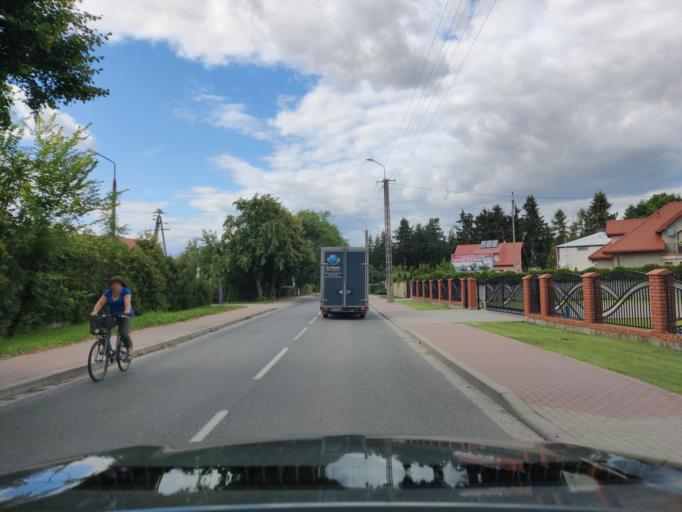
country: PL
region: Masovian Voivodeship
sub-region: Powiat sokolowski
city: Kosow Lacki
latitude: 52.5880
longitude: 22.1517
